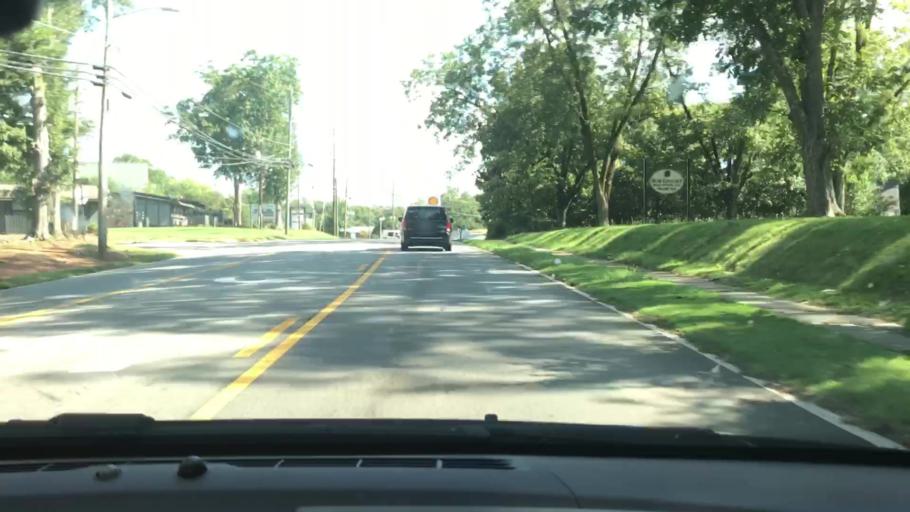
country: US
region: Georgia
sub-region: Troup County
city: La Grange
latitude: 33.0567
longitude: -85.0340
